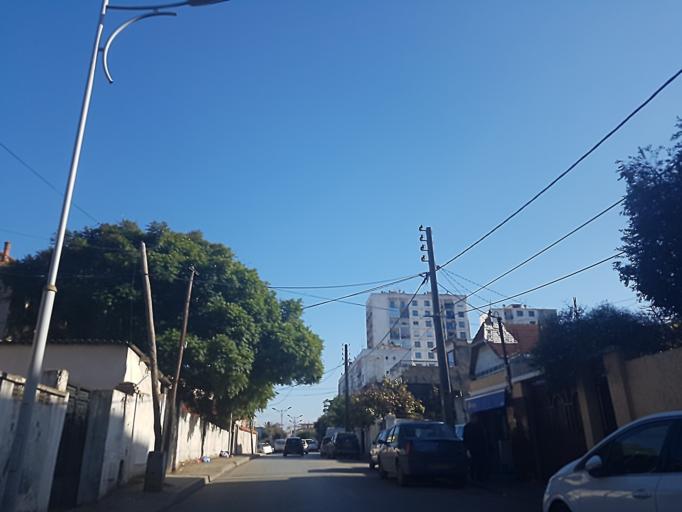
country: DZ
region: Alger
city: Birkhadem
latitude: 36.7355
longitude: 3.0969
